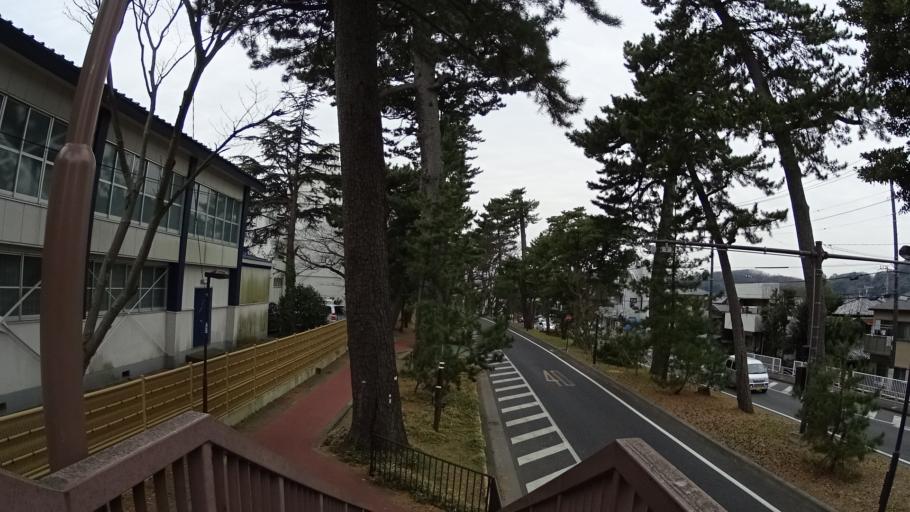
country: JP
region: Kanagawa
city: Oiso
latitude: 35.3079
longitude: 139.3080
